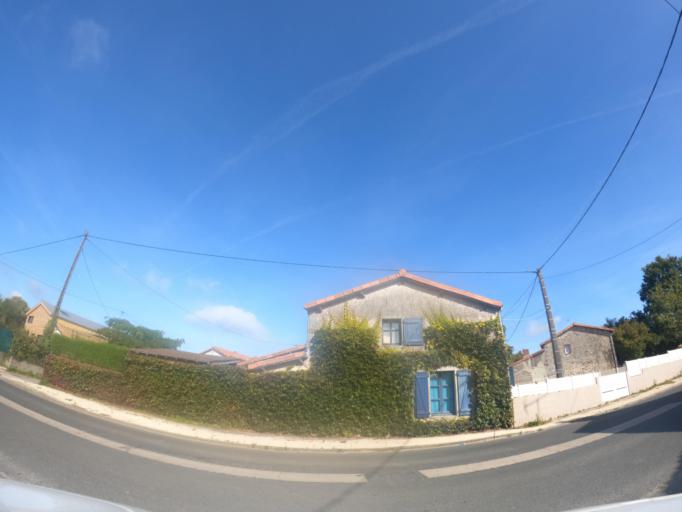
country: FR
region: Poitou-Charentes
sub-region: Departement des Deux-Sevres
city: Courlay
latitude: 46.7862
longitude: -0.5730
